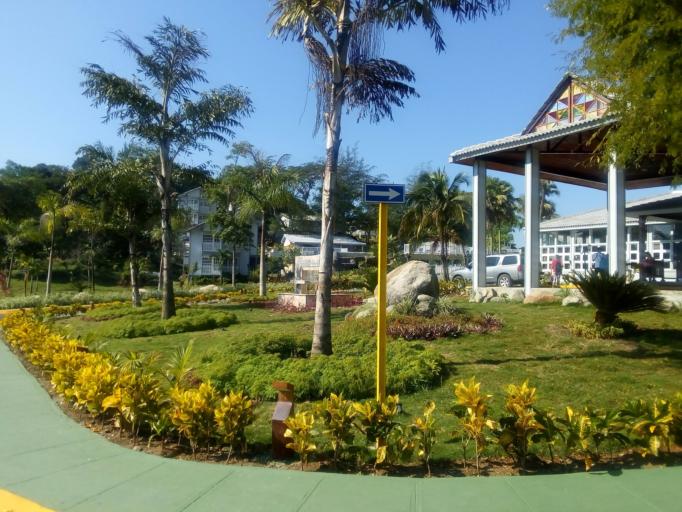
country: CU
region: Santiago de Cuba
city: Segundo Frente
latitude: 20.4268
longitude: -75.5406
